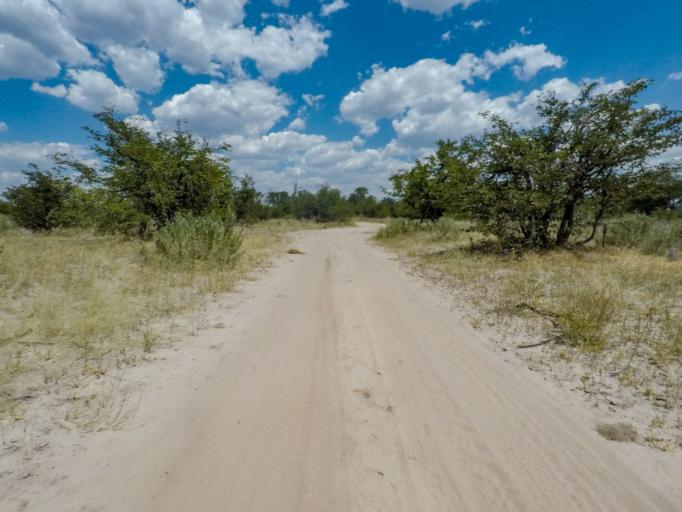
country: BW
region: North West
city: Maun
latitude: -19.1771
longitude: 23.7497
